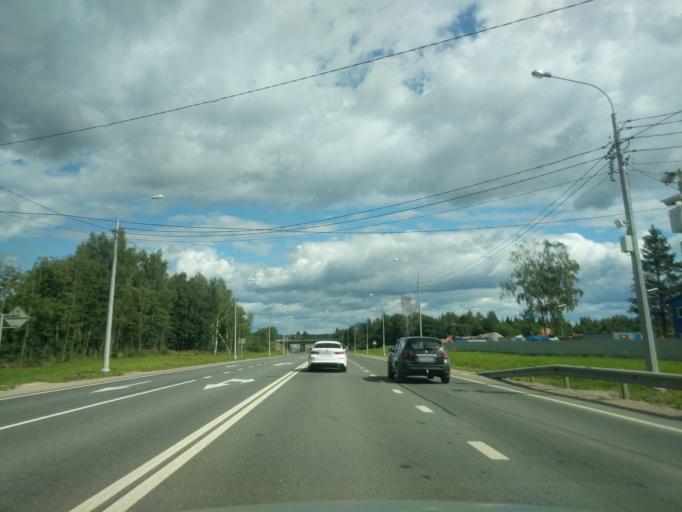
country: RU
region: Kostroma
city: Oktyabr'skiy
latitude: 57.7854
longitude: 41.0529
